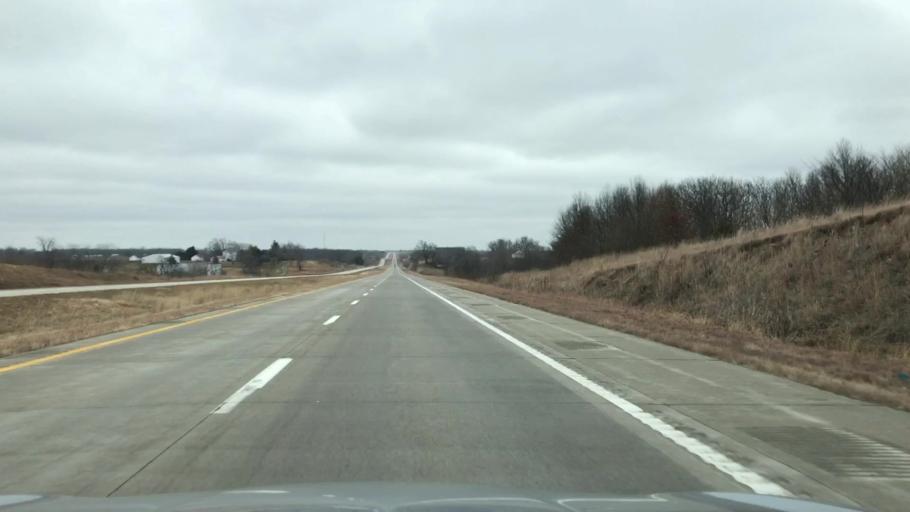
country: US
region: Missouri
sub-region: Caldwell County
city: Hamilton
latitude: 39.7351
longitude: -93.8421
